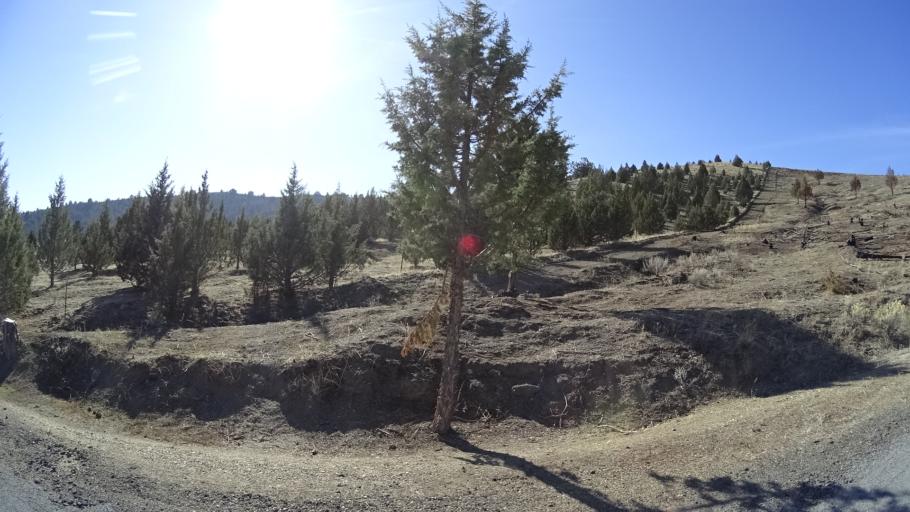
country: US
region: California
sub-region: Siskiyou County
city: Montague
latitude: 41.6328
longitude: -122.5398
